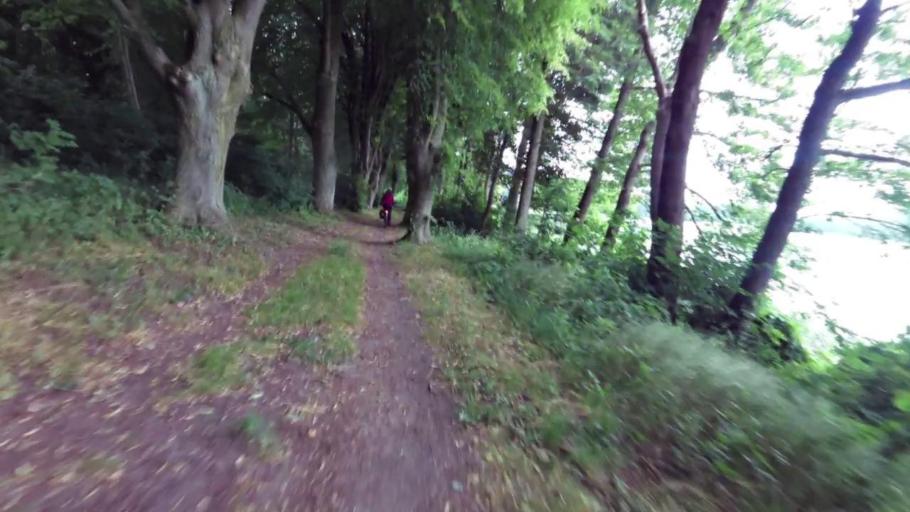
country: PL
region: West Pomeranian Voivodeship
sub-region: Powiat stargardzki
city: Chociwel
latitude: 53.4646
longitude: 15.3482
